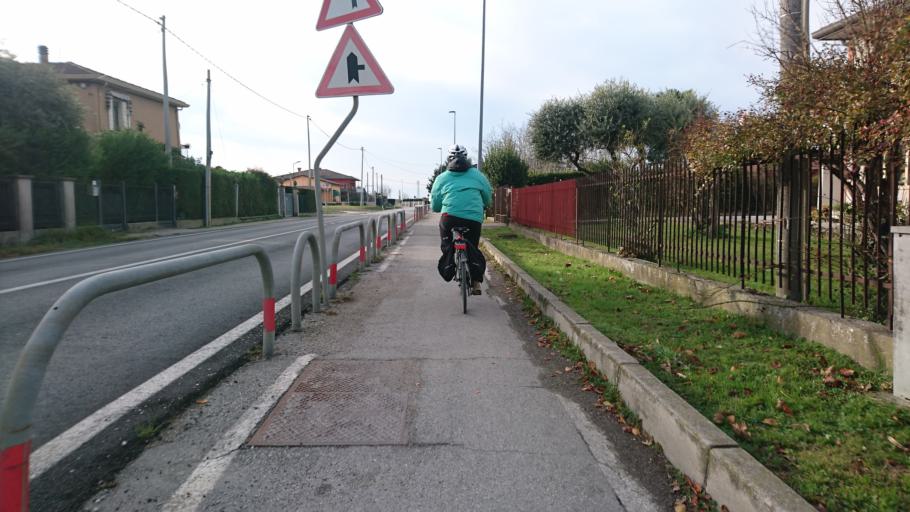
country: IT
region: Veneto
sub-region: Provincia di Padova
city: Polverara
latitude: 45.3223
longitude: 11.9636
